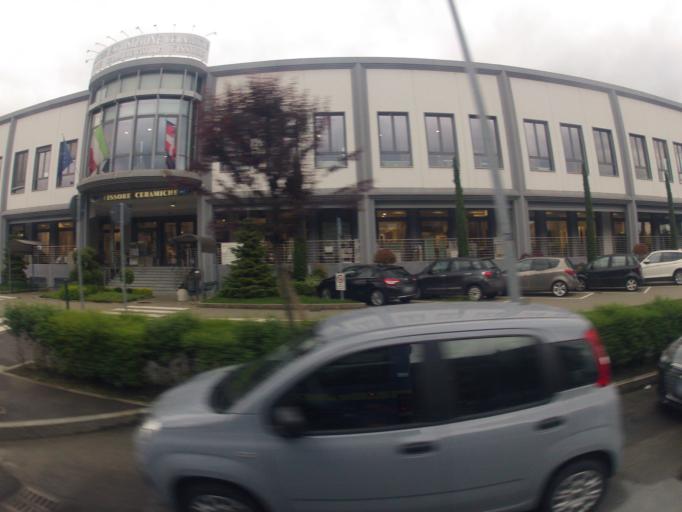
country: IT
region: Piedmont
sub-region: Provincia di Torino
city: Tagliaferro
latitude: 44.9964
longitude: 7.6718
